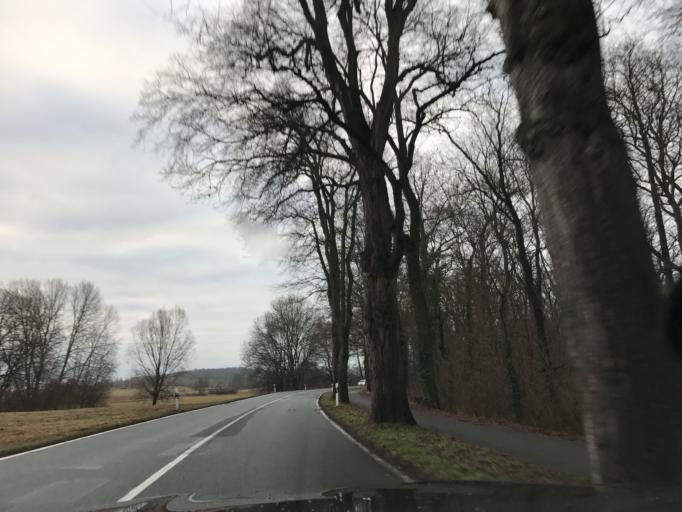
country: DE
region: Brandenburg
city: Werder
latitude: 52.3744
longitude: 12.9579
